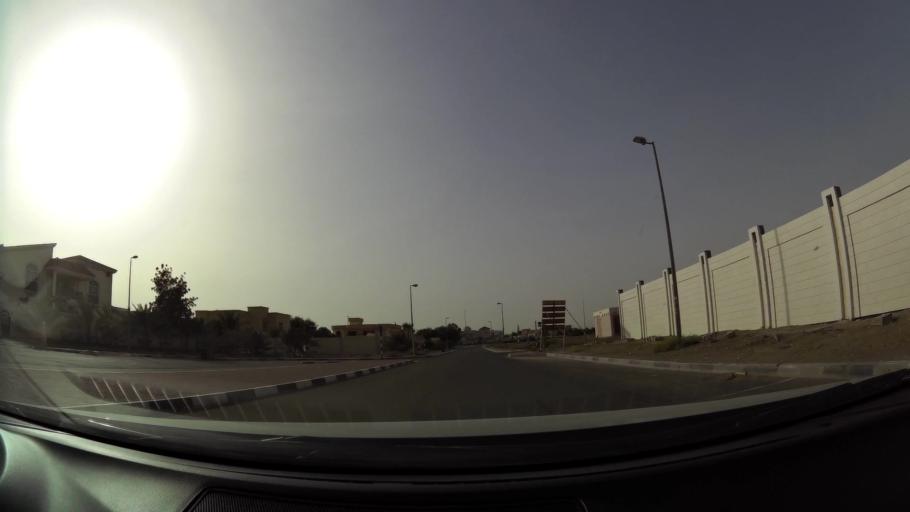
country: AE
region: Abu Dhabi
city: Al Ain
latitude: 24.2220
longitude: 55.6554
